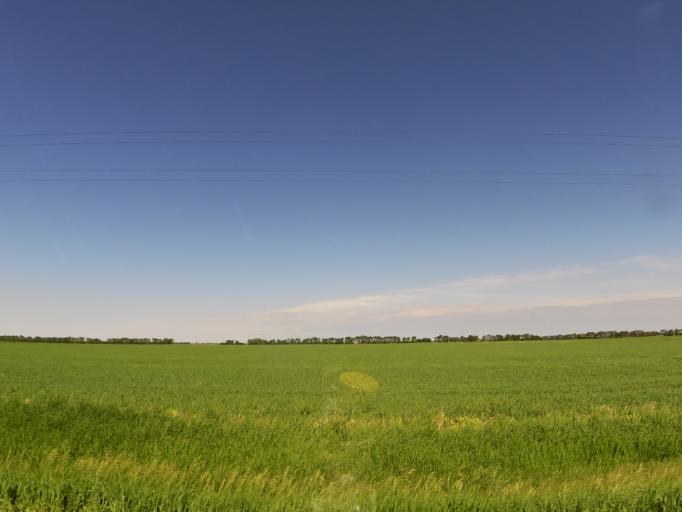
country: US
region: North Dakota
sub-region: Walsh County
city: Grafton
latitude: 48.3217
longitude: -97.2553
